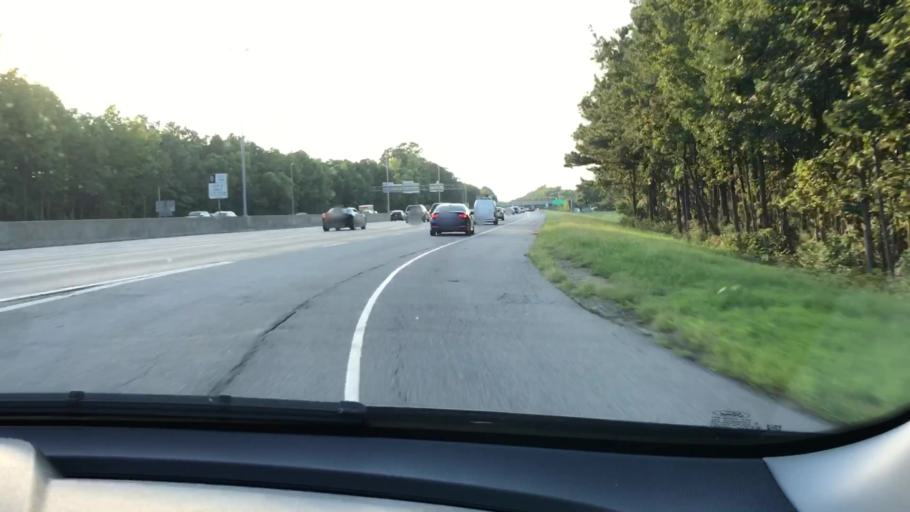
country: US
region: Virginia
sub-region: City of Newport News
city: Newport News
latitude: 37.0591
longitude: -76.4206
